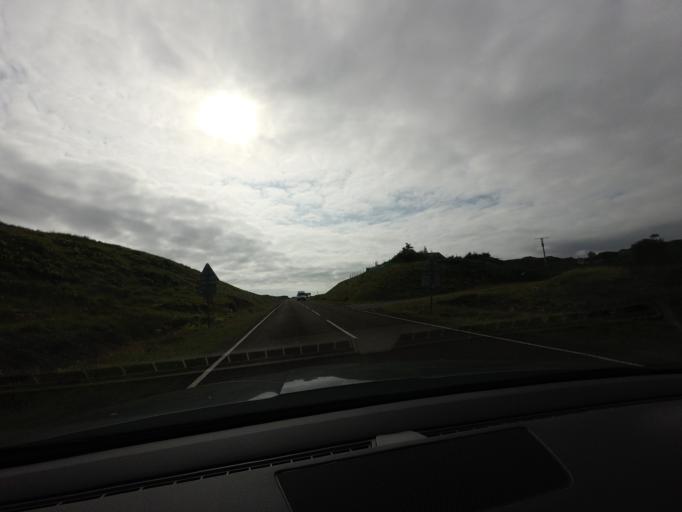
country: GB
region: Scotland
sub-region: Highland
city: Ullapool
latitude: 58.4227
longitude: -4.9945
